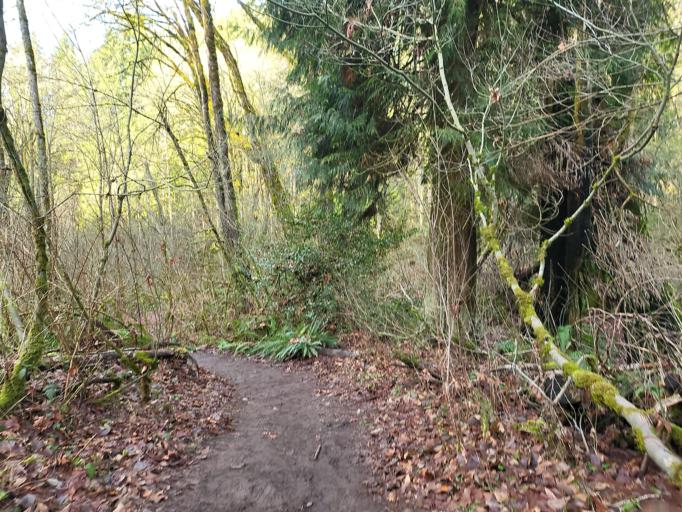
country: US
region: Washington
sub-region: King County
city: Newcastle
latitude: 47.5430
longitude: -122.1484
